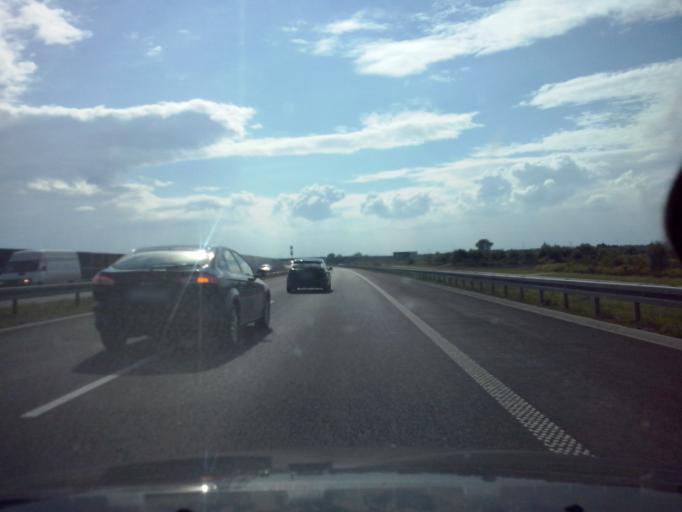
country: PL
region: Lesser Poland Voivodeship
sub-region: Powiat tarnowski
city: Wierzchoslawice
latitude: 50.0493
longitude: 20.9027
